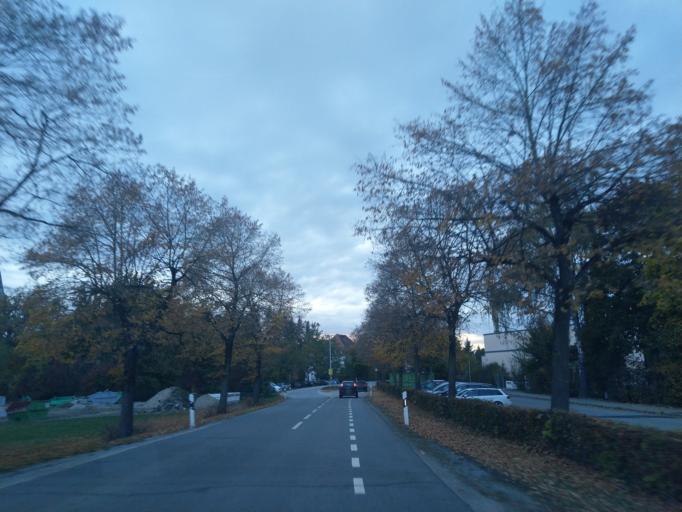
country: DE
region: Bavaria
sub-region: Lower Bavaria
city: Niederalteich
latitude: 48.7652
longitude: 13.0315
